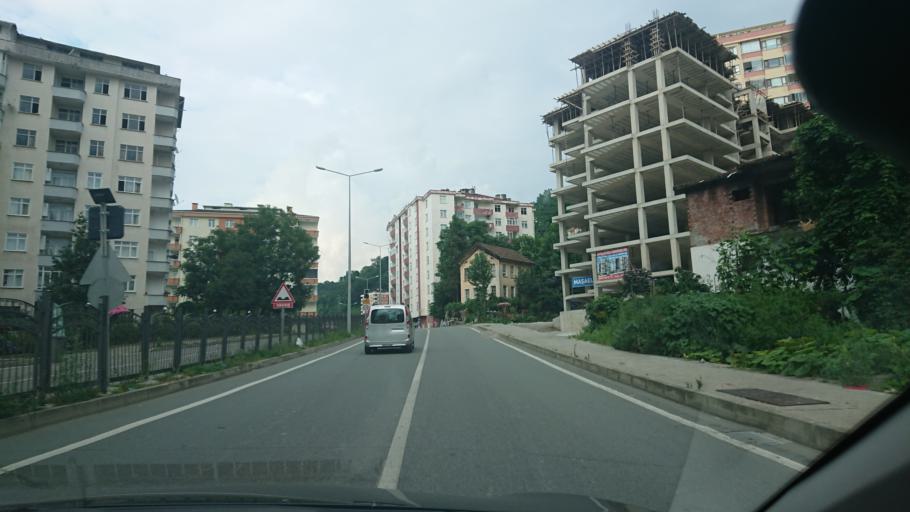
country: TR
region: Rize
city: Rize
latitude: 41.0250
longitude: 40.5459
